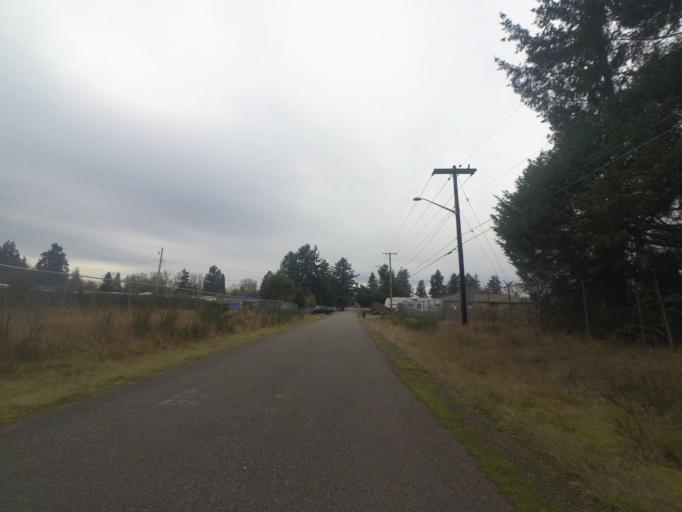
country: US
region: Washington
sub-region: Pierce County
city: McChord Air Force Base
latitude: 47.1249
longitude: -122.5245
